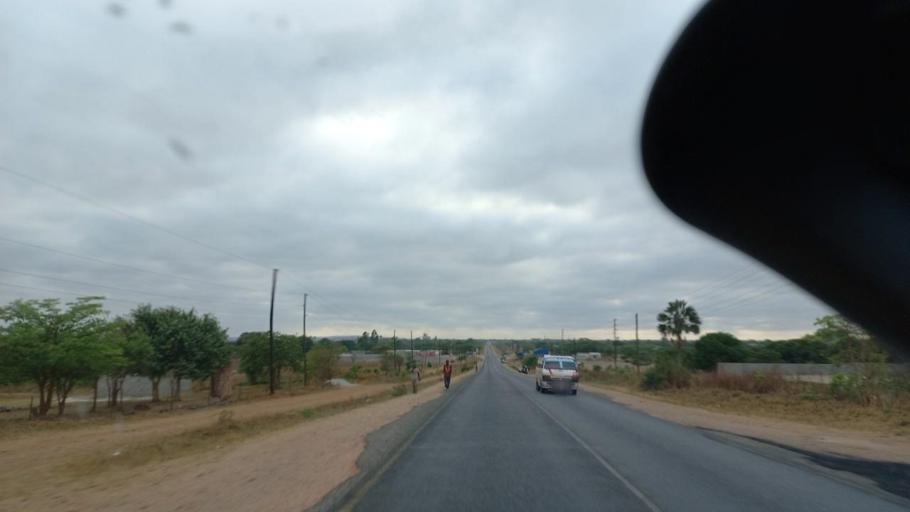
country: ZM
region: Lusaka
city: Chongwe
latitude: -15.3410
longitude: 28.6122
